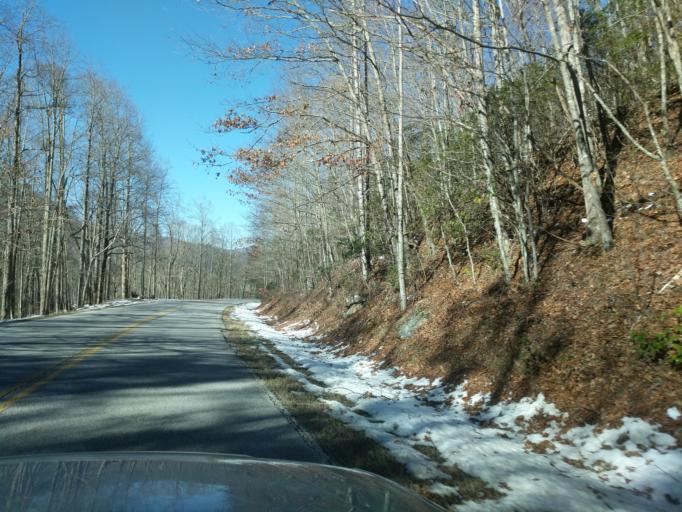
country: US
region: Georgia
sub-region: Towns County
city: Hiawassee
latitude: 34.9145
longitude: -83.6218
